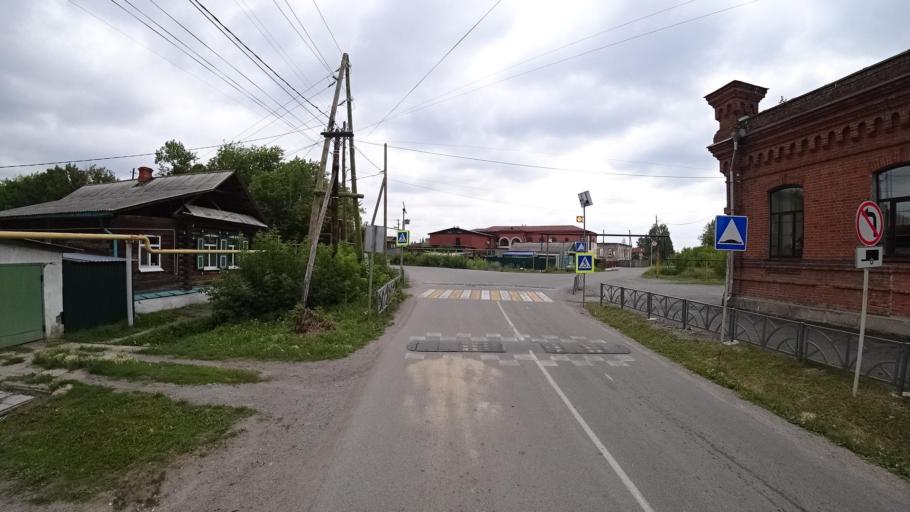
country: RU
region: Sverdlovsk
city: Kamyshlov
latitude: 56.8425
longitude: 62.7011
